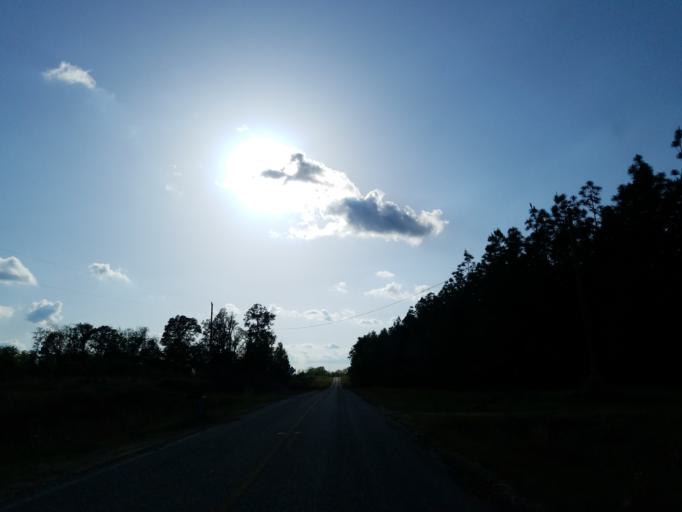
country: US
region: Georgia
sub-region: Turner County
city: Ashburn
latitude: 31.6083
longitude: -83.5903
